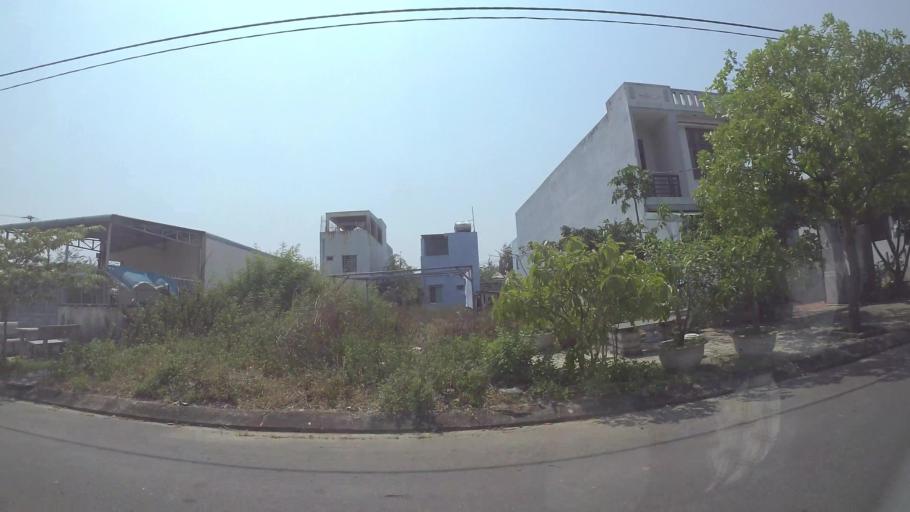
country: VN
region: Da Nang
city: Ngu Hanh Son
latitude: 15.9878
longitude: 108.2696
